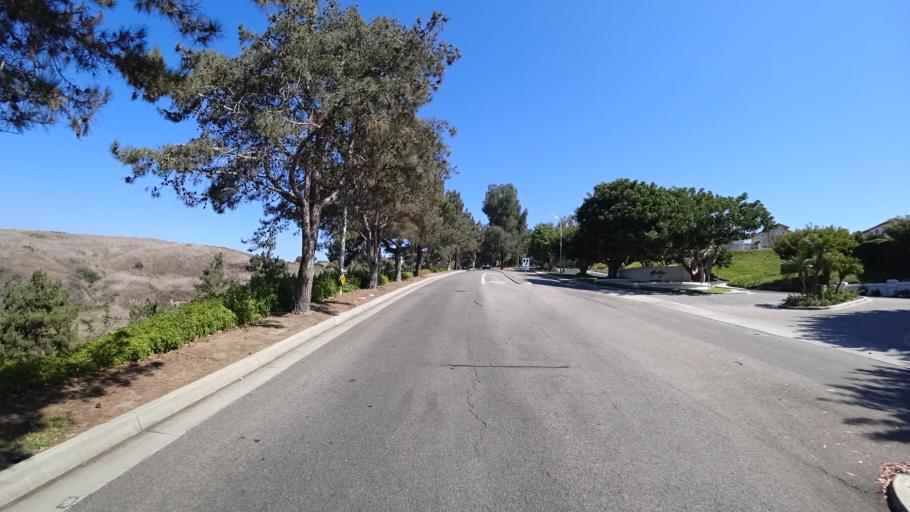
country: US
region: California
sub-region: Orange County
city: San Clemente
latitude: 33.4444
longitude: -117.6047
